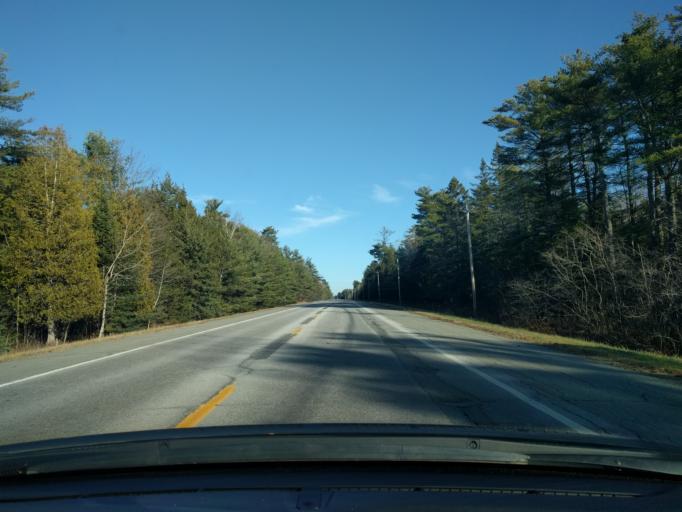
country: US
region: Maine
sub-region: Penobscot County
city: Hampden
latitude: 44.7603
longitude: -68.8270
